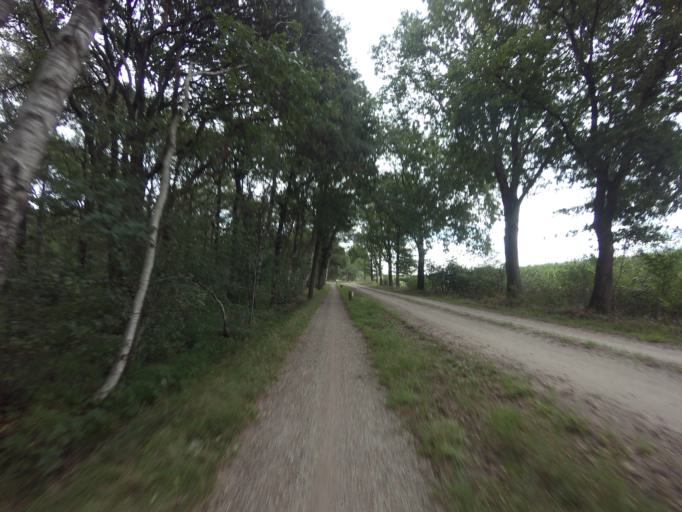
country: NL
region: Gelderland
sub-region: Gemeente Lochem
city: Laren
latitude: 52.2977
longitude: 6.3731
